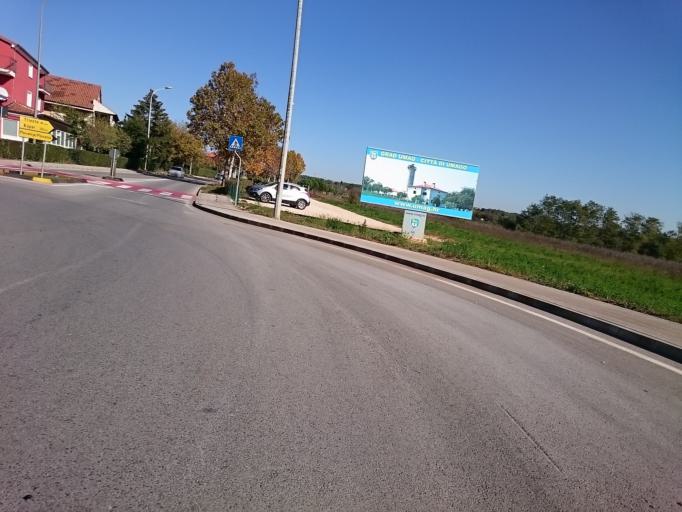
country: HR
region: Istarska
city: Umag
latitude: 45.4394
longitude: 13.5322
